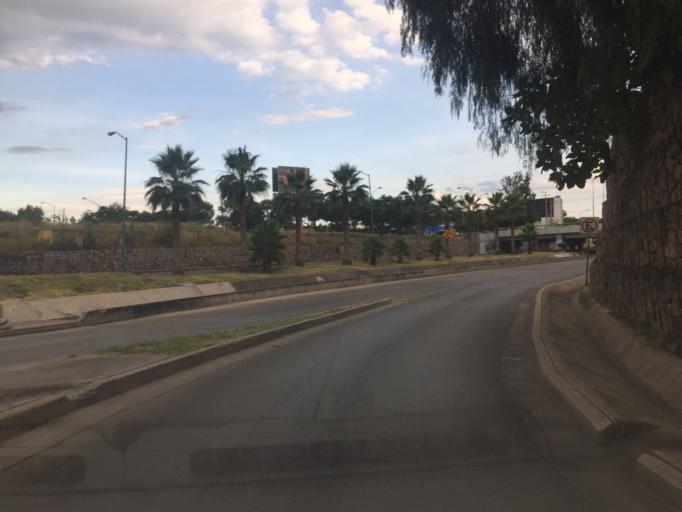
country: MX
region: Guanajuato
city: Leon
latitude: 21.1486
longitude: -101.6789
